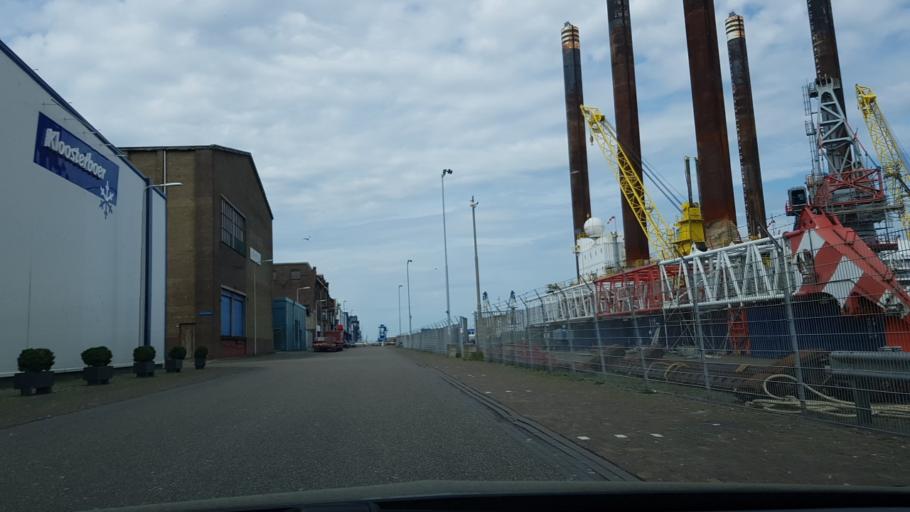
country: NL
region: North Holland
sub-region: Gemeente Velsen
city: Velsen-Zuid
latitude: 52.4599
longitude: 4.5875
